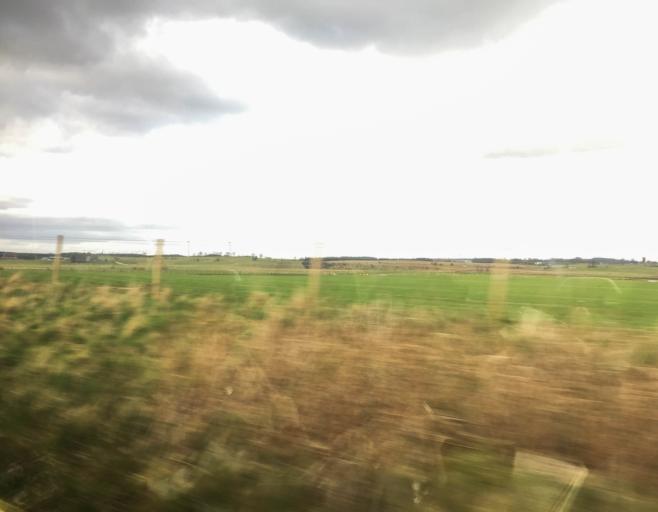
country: GB
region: Scotland
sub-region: South Lanarkshire
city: Carnwath
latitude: 55.6754
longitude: -3.6459
